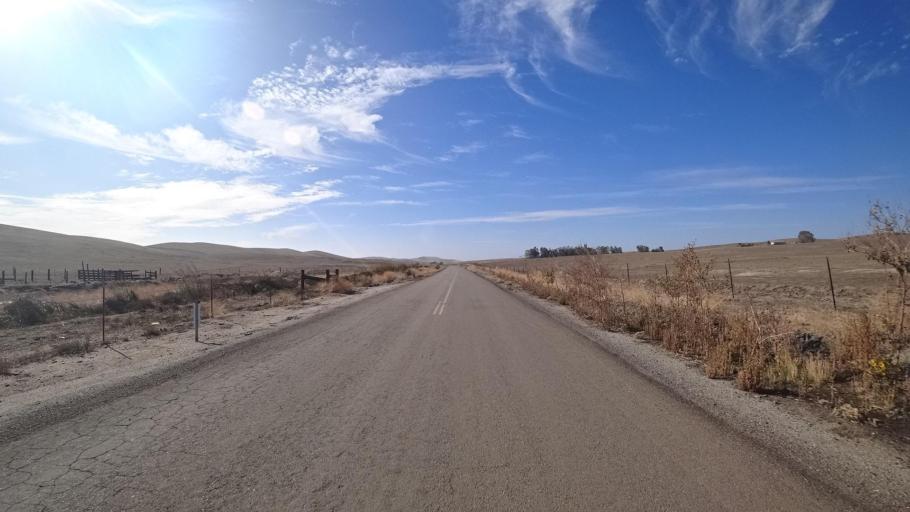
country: US
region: California
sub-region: Tulare County
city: Richgrove
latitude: 35.6321
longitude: -118.9625
